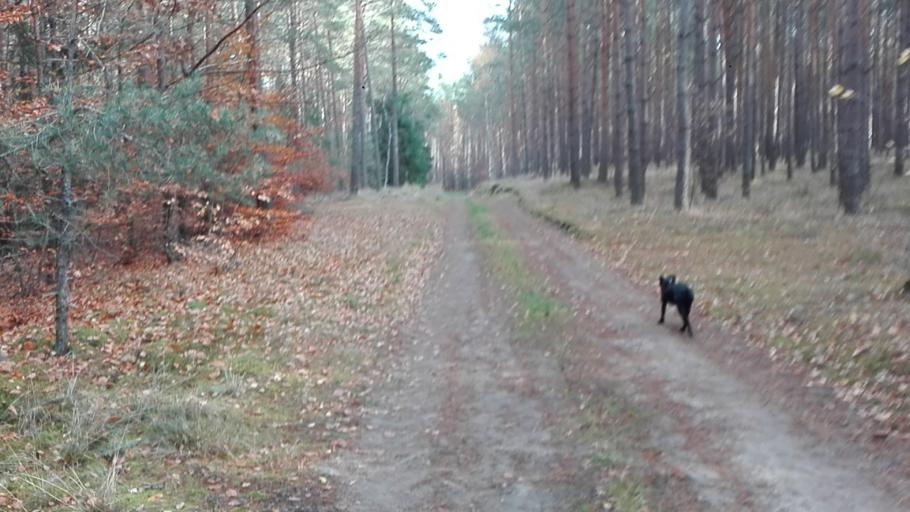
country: PL
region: West Pomeranian Voivodeship
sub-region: Powiat szczecinecki
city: Barwice
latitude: 53.8038
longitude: 16.3729
